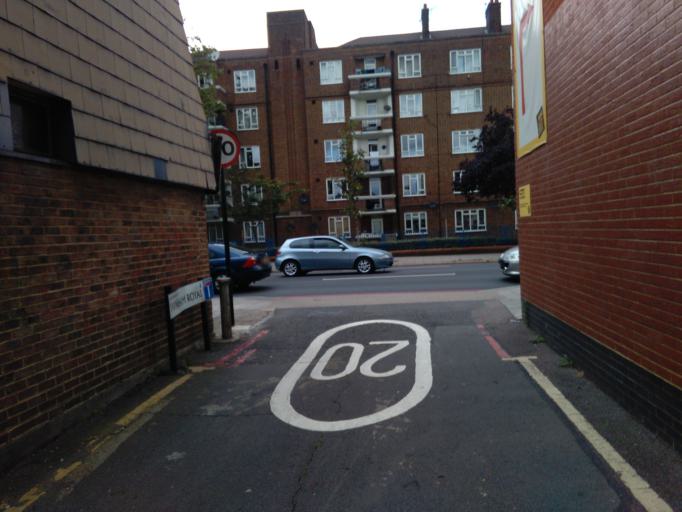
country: GB
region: England
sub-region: Greater London
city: Lambeth
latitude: 51.4865
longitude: -0.1170
